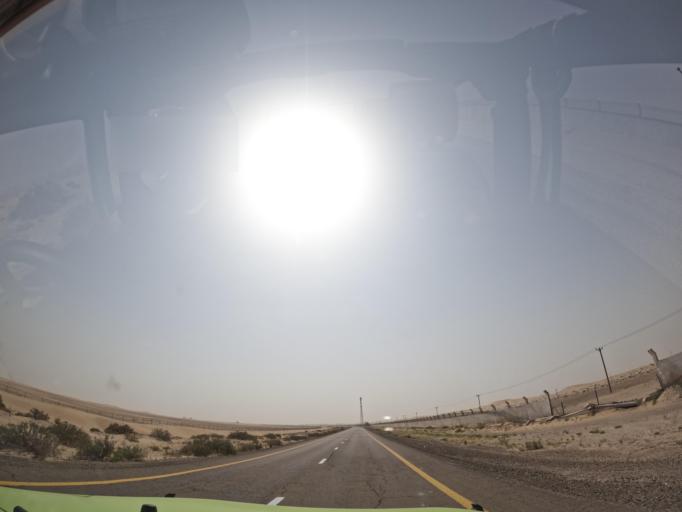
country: AE
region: Dubai
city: Dubai
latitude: 24.6150
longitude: 55.2984
